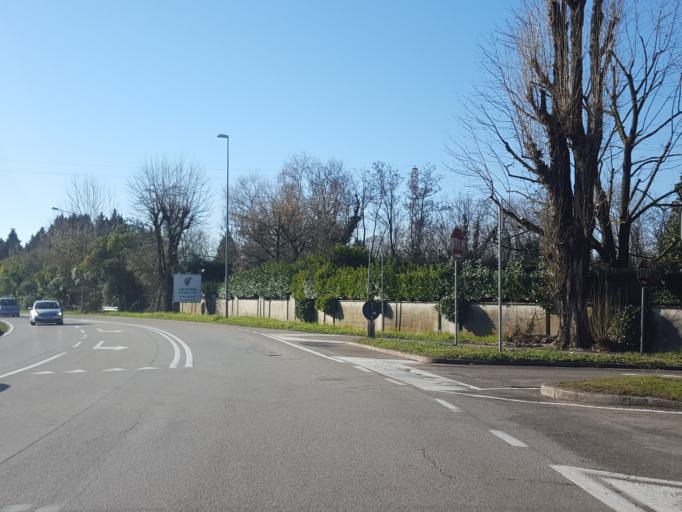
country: IT
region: Veneto
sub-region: Provincia di Vicenza
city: Vicenza
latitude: 45.5706
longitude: 11.5468
